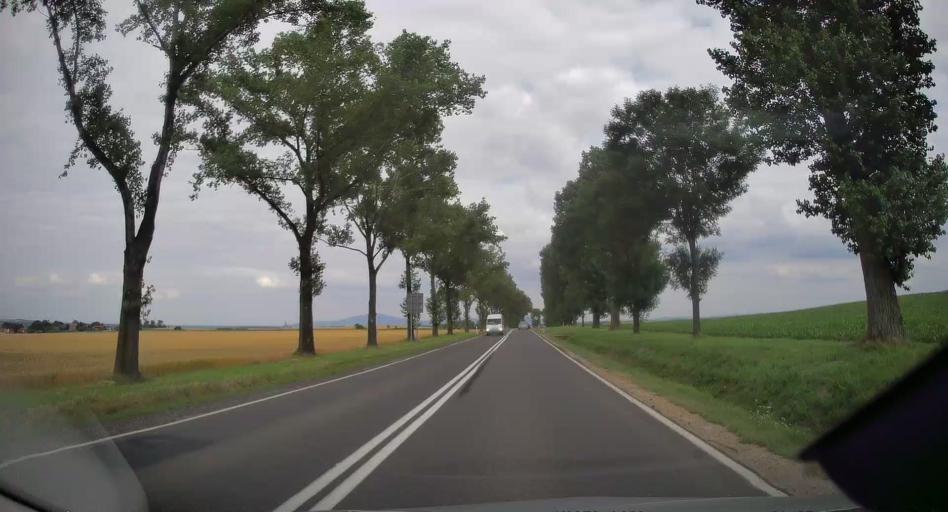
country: PL
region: Lower Silesian Voivodeship
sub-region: Powiat swidnicki
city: Swiebodzice
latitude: 50.8383
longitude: 16.4022
